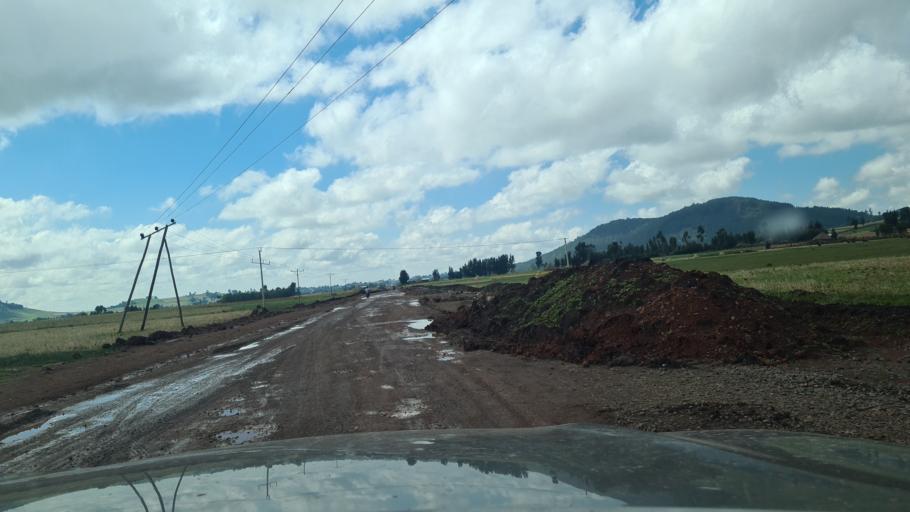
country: ET
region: Oromiya
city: Huruta
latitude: 8.0917
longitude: 39.5373
